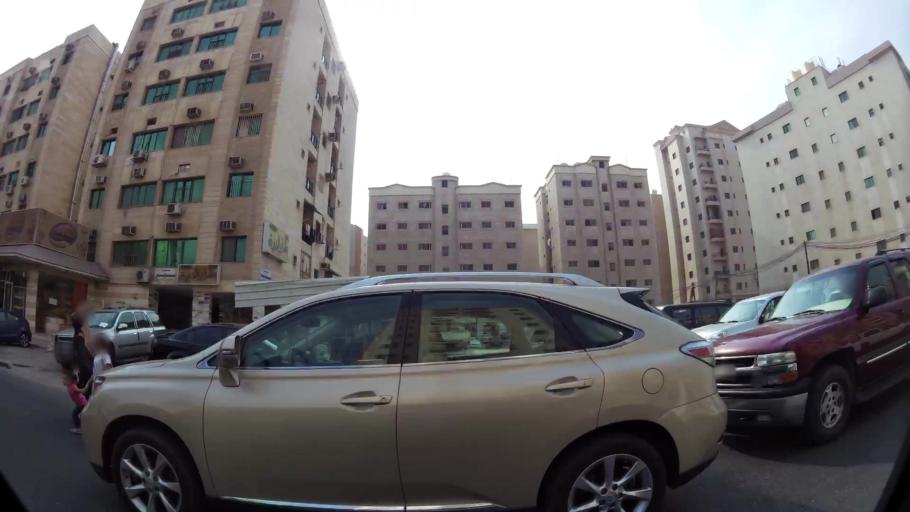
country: KW
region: Al Farwaniyah
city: Al Farwaniyah
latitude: 29.2773
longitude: 47.9546
